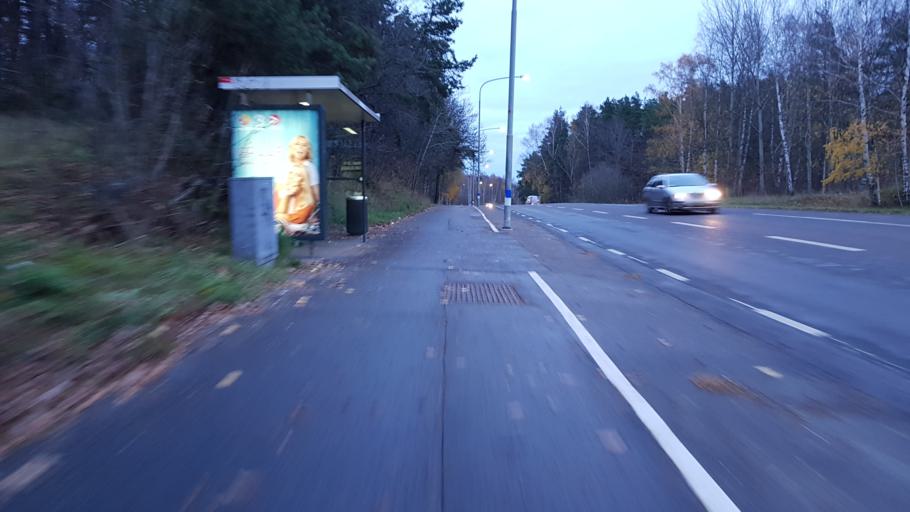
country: SE
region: OEstergoetland
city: Lindo
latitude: 58.5951
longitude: 16.2317
